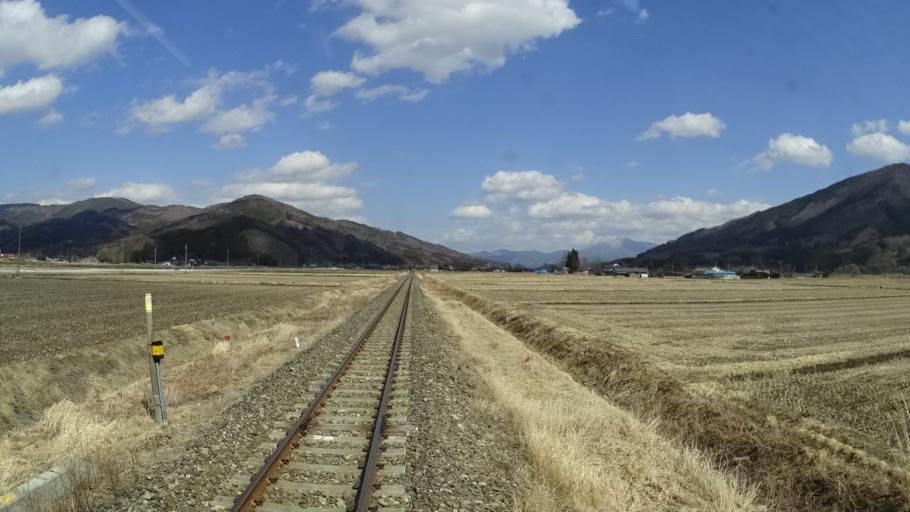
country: JP
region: Iwate
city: Tono
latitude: 39.3265
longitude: 141.4675
